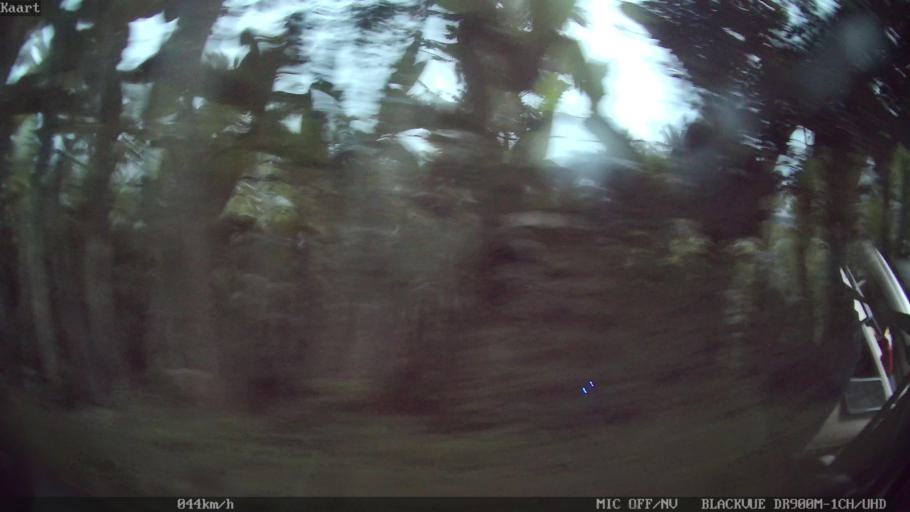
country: ID
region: Bali
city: Banjar Taro Kelod
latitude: -8.3499
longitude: 115.2777
